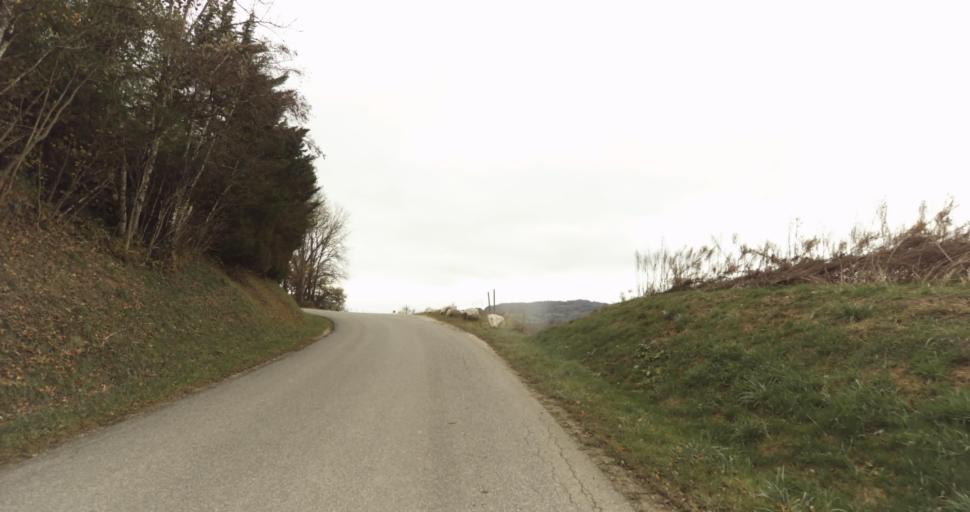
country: FR
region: Rhone-Alpes
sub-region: Departement de la Haute-Savoie
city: Groisy
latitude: 45.9945
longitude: 6.1812
